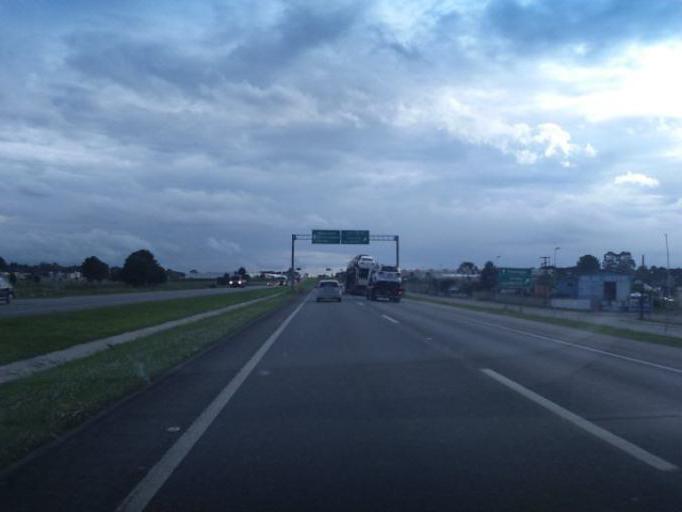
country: BR
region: Parana
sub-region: Piraquara
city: Piraquara
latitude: -25.5058
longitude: -49.1239
